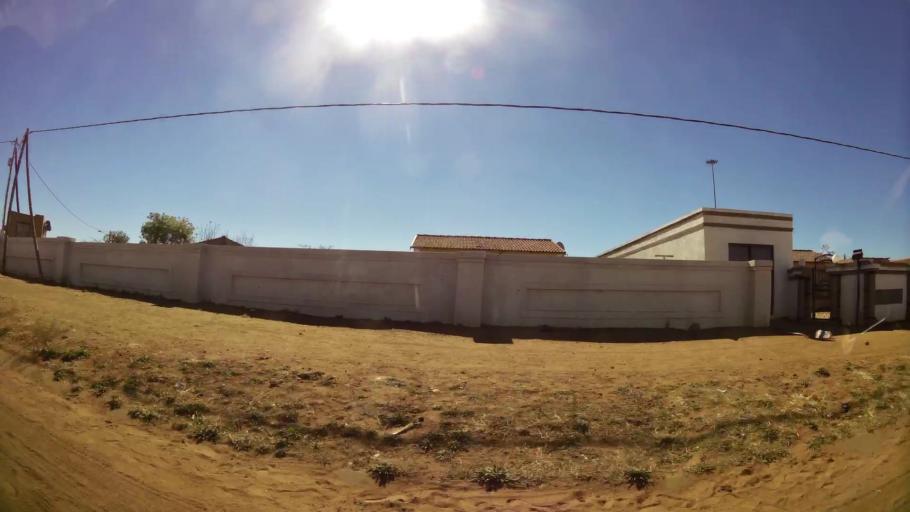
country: ZA
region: North-West
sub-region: Dr Kenneth Kaunda District Municipality
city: Klerksdorp
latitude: -26.8679
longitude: 26.5727
